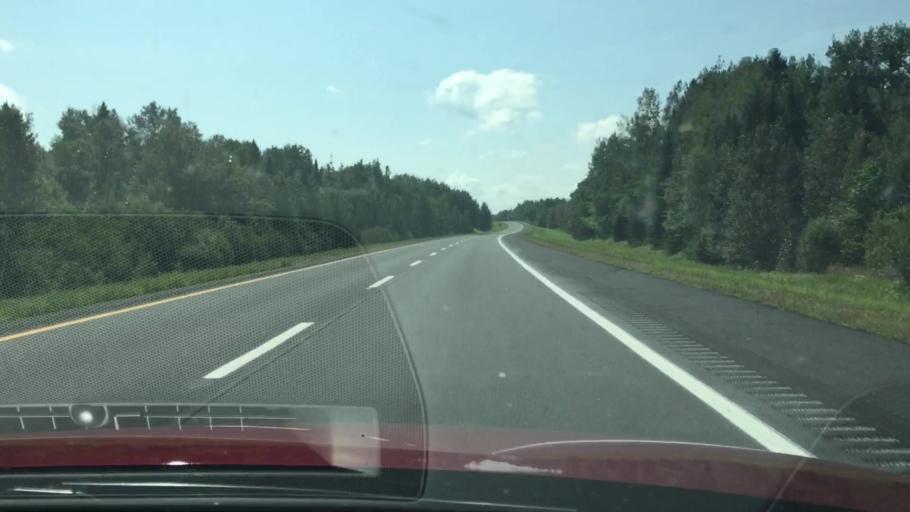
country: US
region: Maine
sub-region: Penobscot County
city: Patten
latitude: 45.9178
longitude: -68.3722
